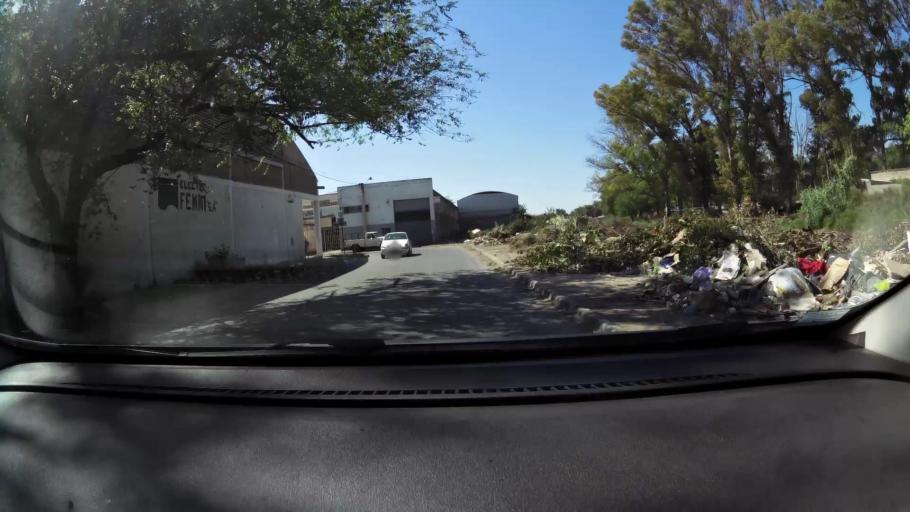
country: AR
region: Cordoba
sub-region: Departamento de Capital
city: Cordoba
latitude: -31.4356
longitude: -64.1333
